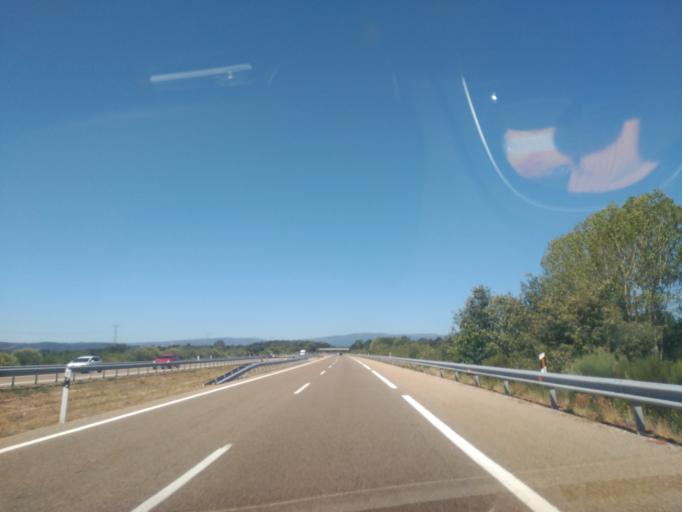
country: ES
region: Castille and Leon
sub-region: Provincia de Zamora
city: Asturianos
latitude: 42.0433
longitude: -6.4742
